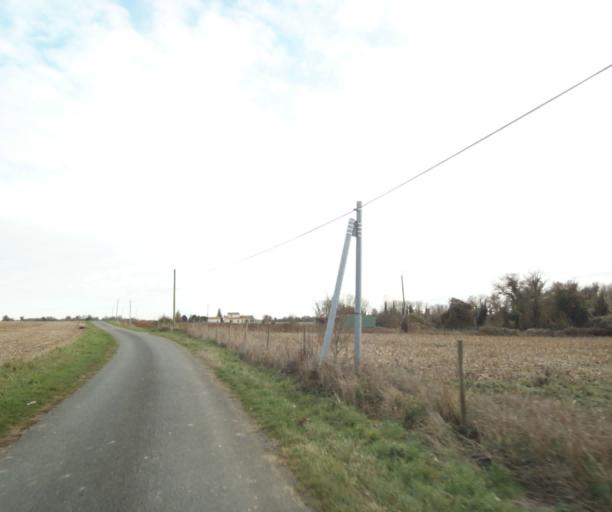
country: FR
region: Poitou-Charentes
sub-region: Departement de la Charente-Maritime
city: Corme-Royal
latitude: 45.7812
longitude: -0.8160
